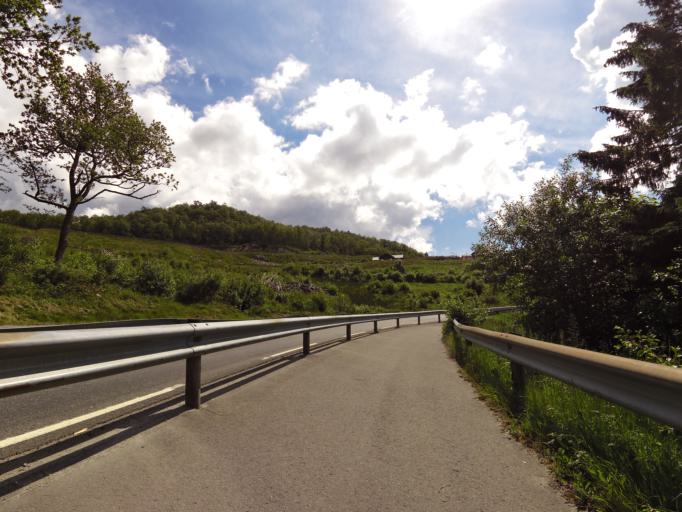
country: NO
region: Vest-Agder
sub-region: Lyngdal
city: Lyngdal
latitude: 58.1160
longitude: 7.0637
